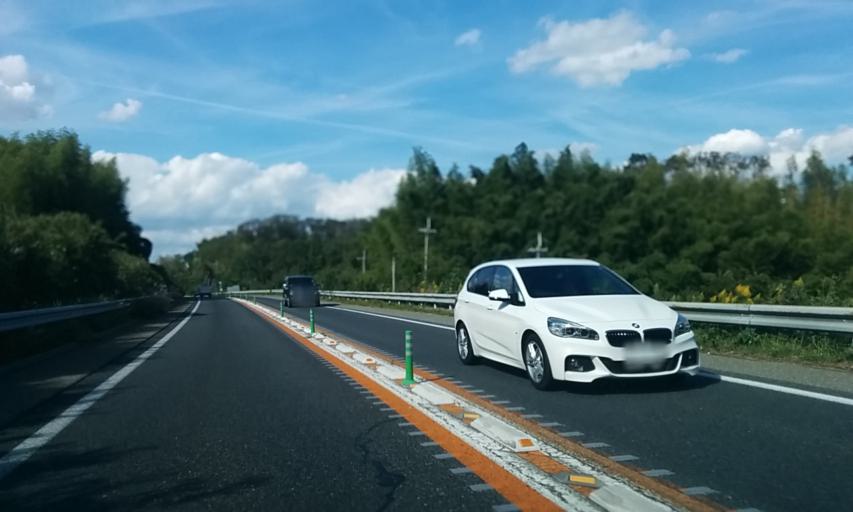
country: JP
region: Kyoto
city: Tanabe
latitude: 34.7641
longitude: 135.7776
